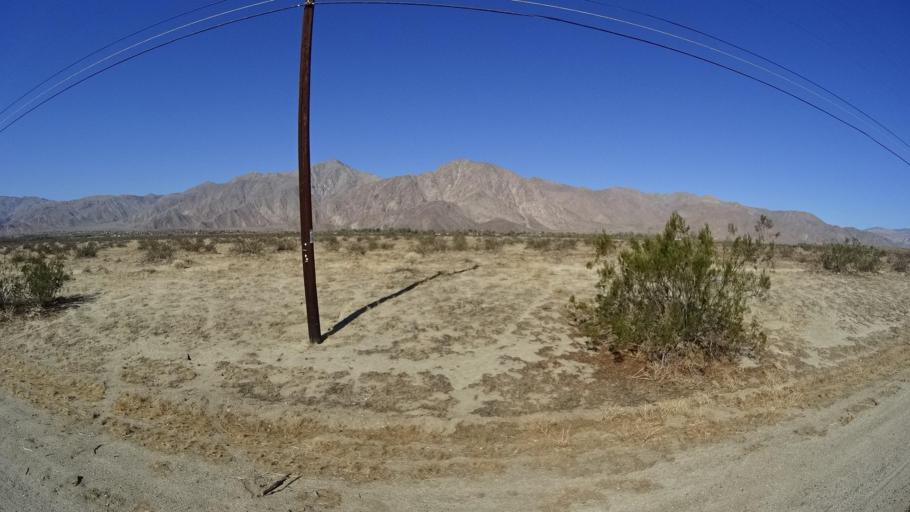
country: US
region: California
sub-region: San Diego County
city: Borrego Springs
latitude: 33.2891
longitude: -116.3664
